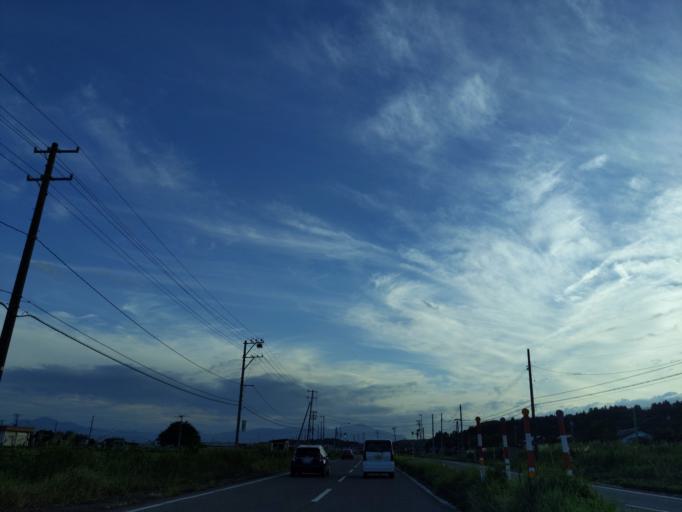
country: JP
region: Niigata
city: Kashiwazaki
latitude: 37.4402
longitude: 138.6299
